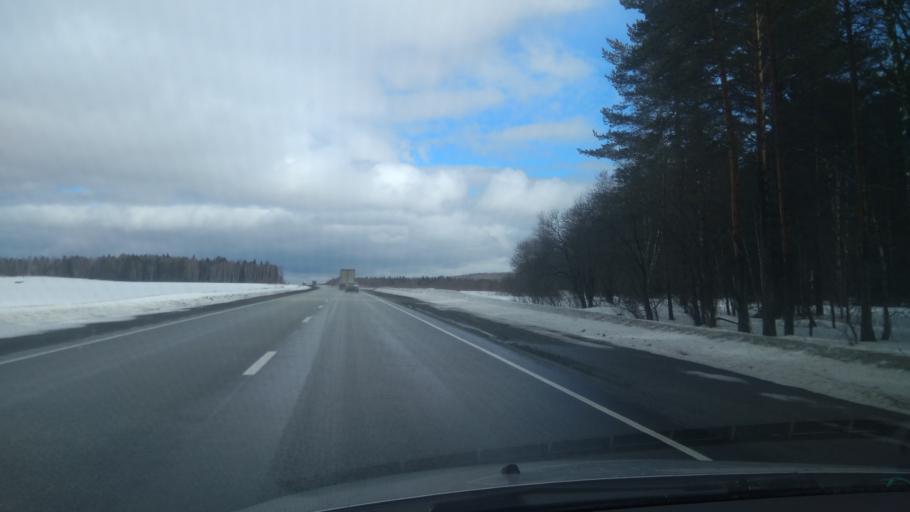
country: RU
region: Sverdlovsk
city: Bisert'
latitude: 56.8097
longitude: 58.7305
